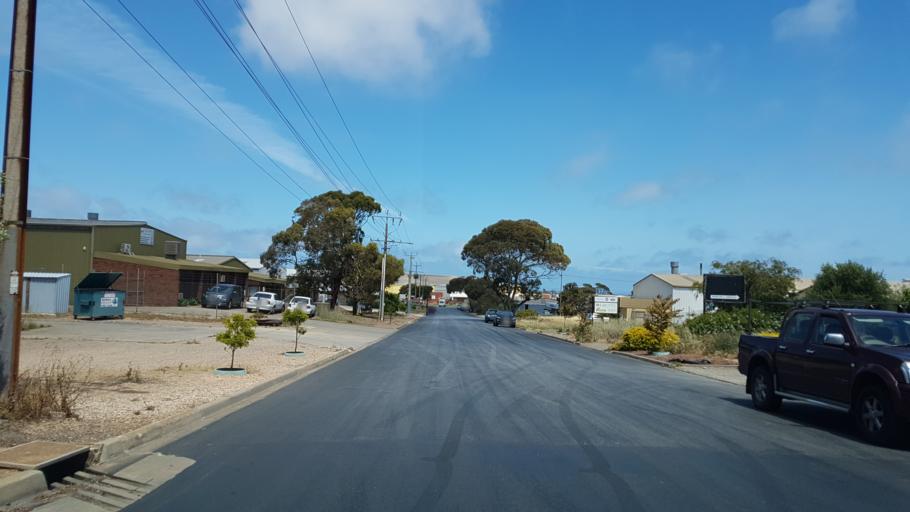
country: AU
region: South Australia
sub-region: Onkaparinga
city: Morphett Vale
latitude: -35.1133
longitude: 138.4999
